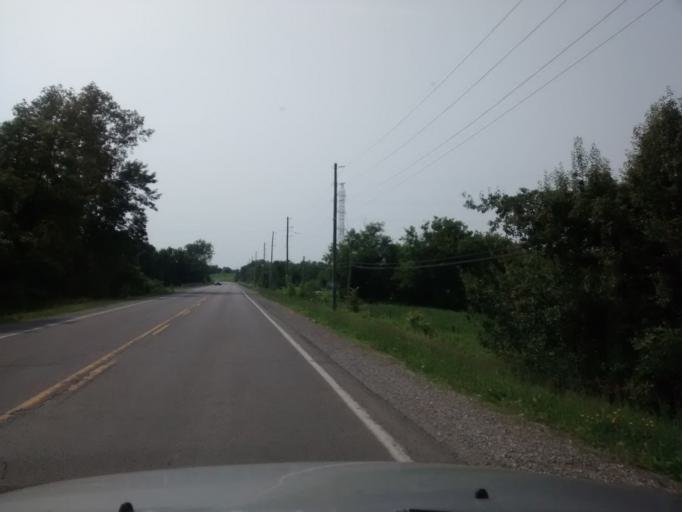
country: CA
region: Ontario
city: Ancaster
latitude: 43.0601
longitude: -79.9173
